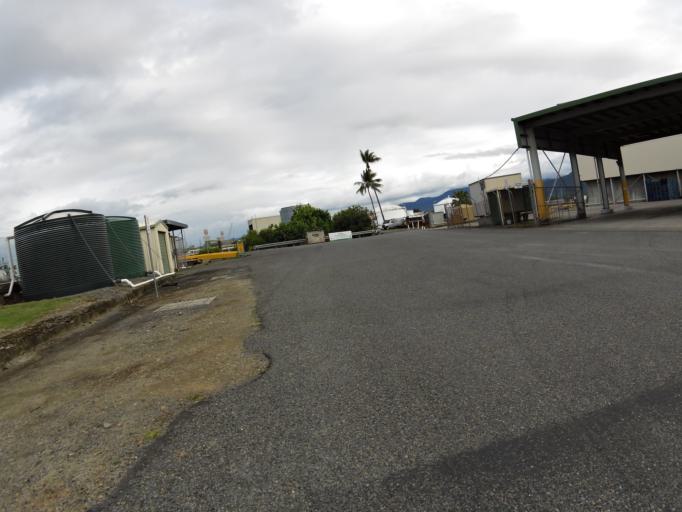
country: AU
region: Queensland
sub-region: Cairns
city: Cairns
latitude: -16.9318
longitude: 145.7792
